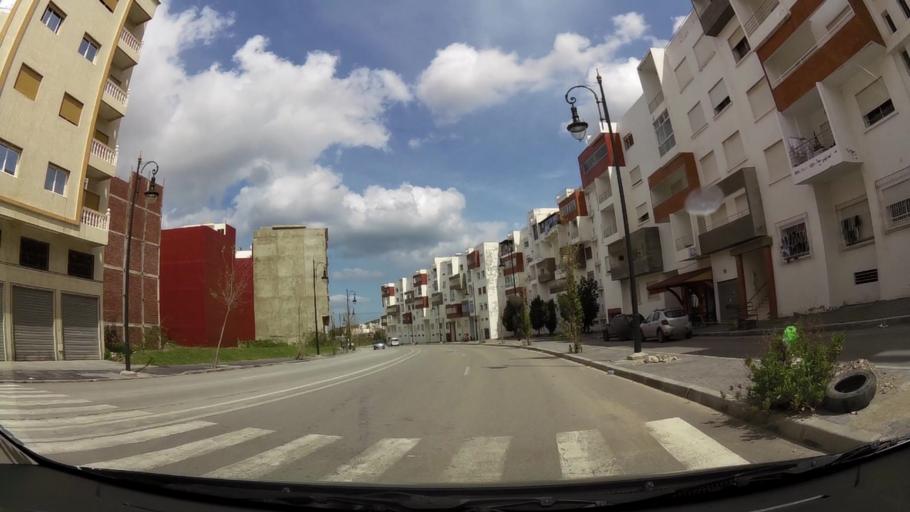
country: MA
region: Tanger-Tetouan
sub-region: Tanger-Assilah
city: Tangier
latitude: 35.7621
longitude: -5.7553
